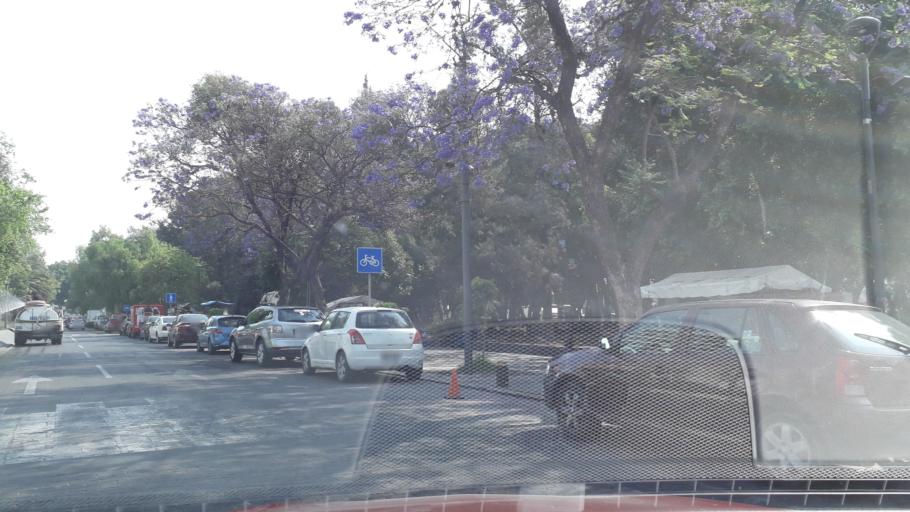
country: MX
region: Puebla
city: Puebla
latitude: 19.0466
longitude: -98.2085
